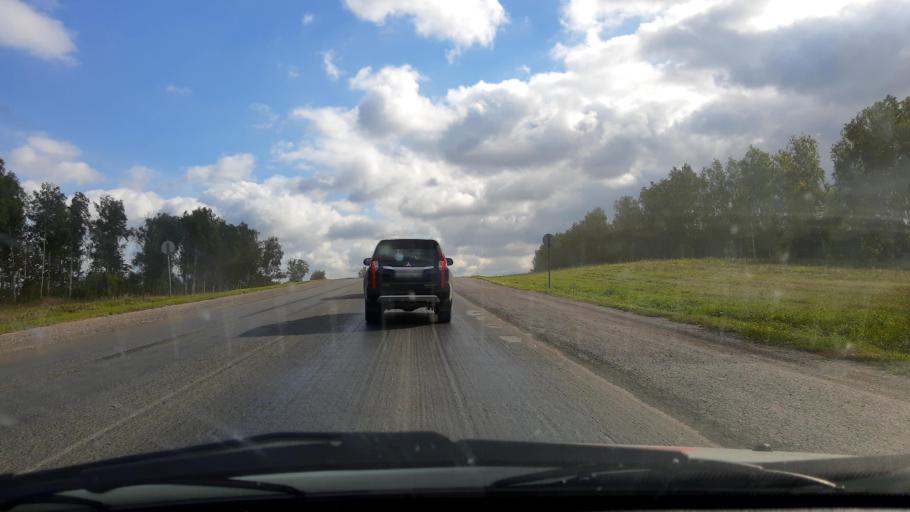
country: RU
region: Bashkortostan
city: Kandry
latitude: 54.5460
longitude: 54.1541
